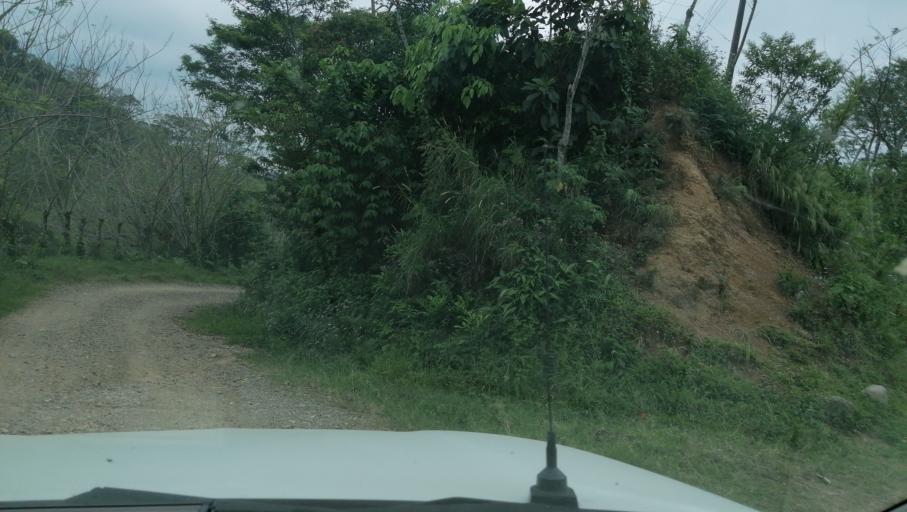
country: MX
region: Chiapas
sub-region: Francisco Leon
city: San Miguel la Sardina
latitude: 17.3408
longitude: -93.3112
